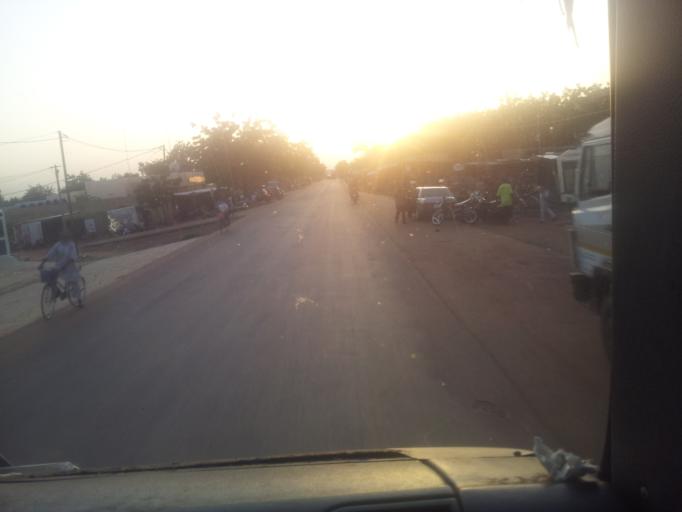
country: BF
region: Centre-Est
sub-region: Kouritenga Province
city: Koupela
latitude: 12.1825
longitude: -0.3554
